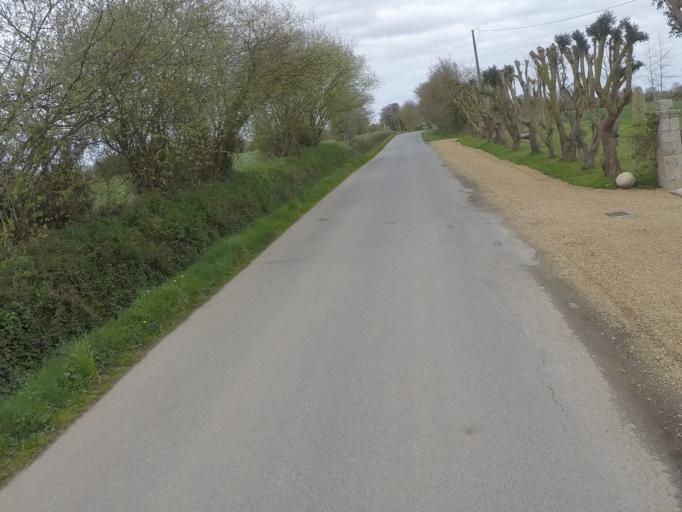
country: FR
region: Brittany
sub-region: Departement des Cotes-d'Armor
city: Plouha
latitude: 48.7069
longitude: -2.9545
